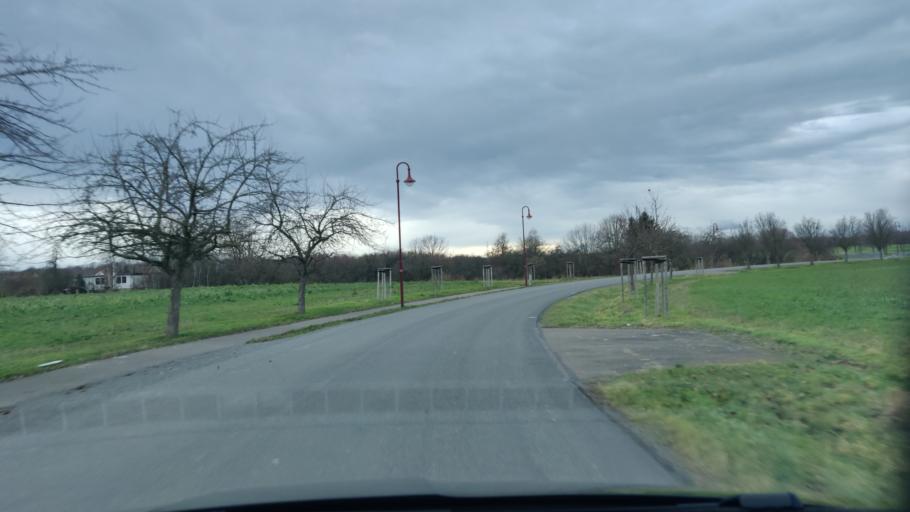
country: DE
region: Saxony
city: Bad Lausick
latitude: 51.1545
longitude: 12.6572
